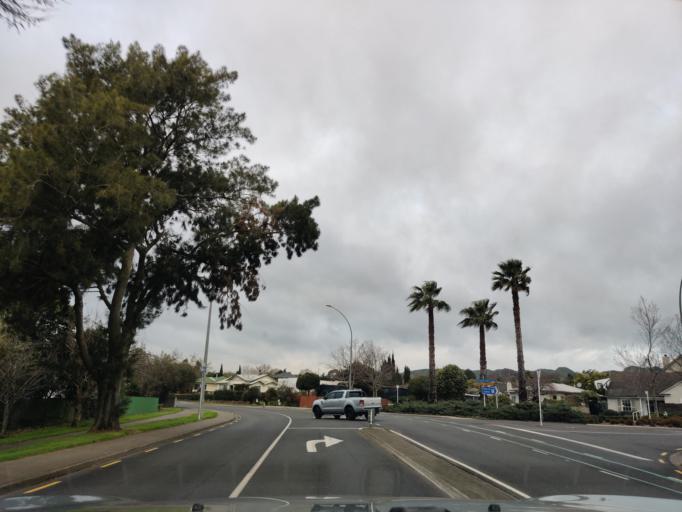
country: NZ
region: Hawke's Bay
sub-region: Hastings District
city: Hastings
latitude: -39.6682
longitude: 176.8813
